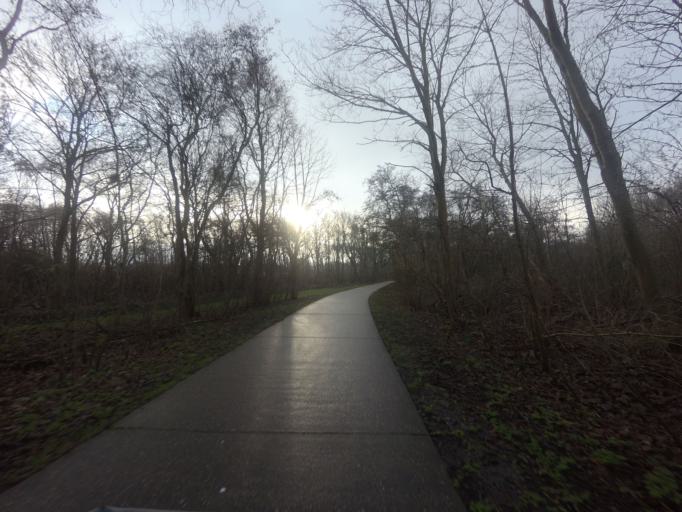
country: NL
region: North Holland
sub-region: Gemeente Texel
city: Den Burg
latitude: 53.1579
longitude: 4.8488
